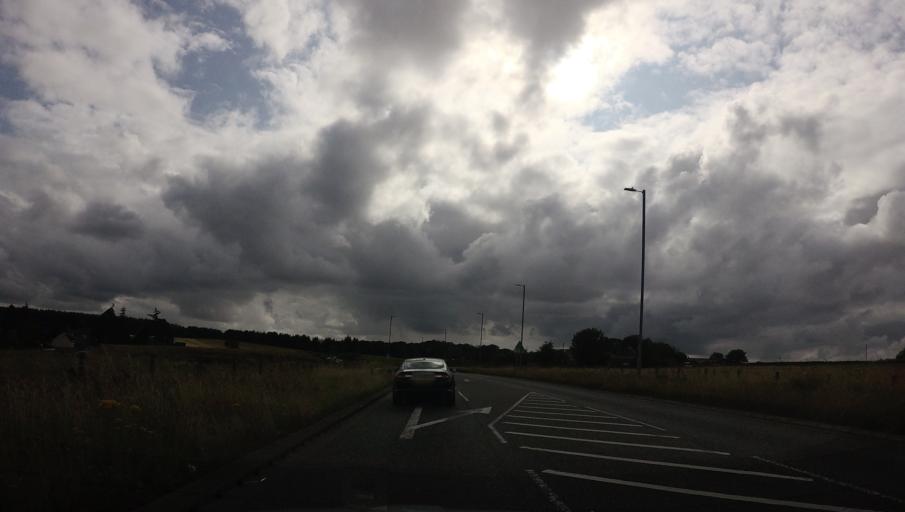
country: GB
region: Scotland
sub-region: Aberdeen City
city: Cults
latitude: 57.1488
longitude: -2.1987
